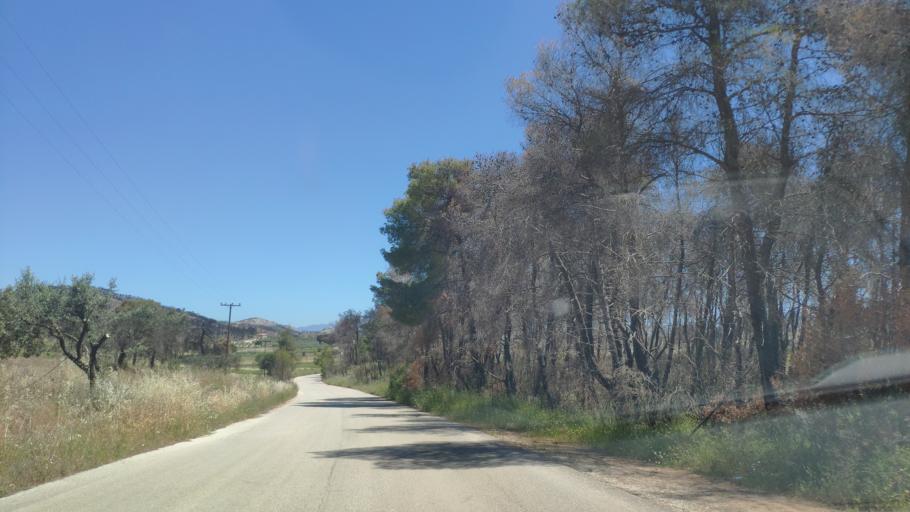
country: GR
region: Peloponnese
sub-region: Nomos Korinthias
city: Athikia
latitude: 37.8406
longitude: 22.9458
